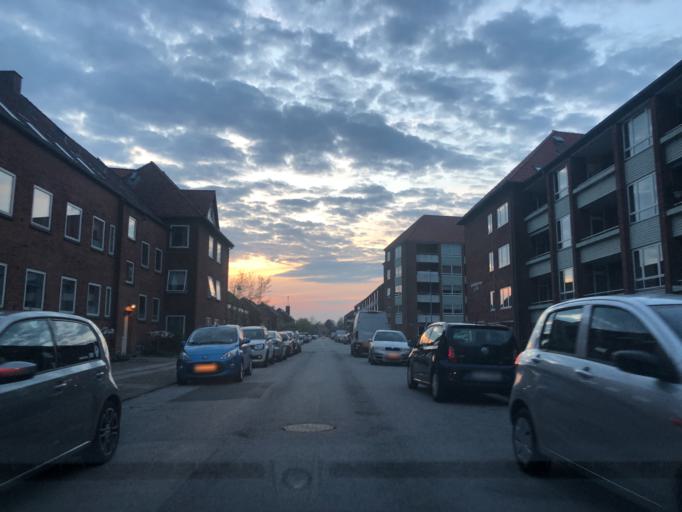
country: DK
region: Zealand
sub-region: Ringsted Kommune
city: Ringsted
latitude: 55.4393
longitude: 11.7887
